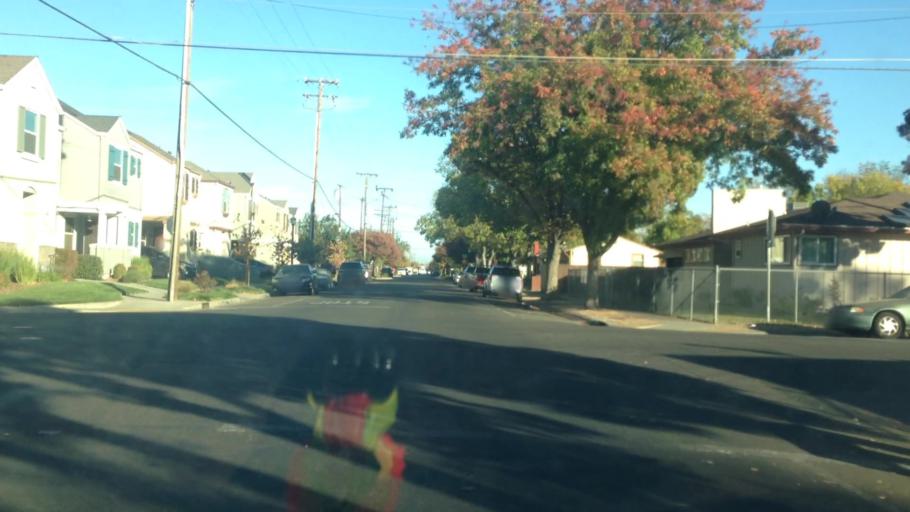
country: US
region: California
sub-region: Sacramento County
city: Sacramento
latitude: 38.6094
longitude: -121.4464
